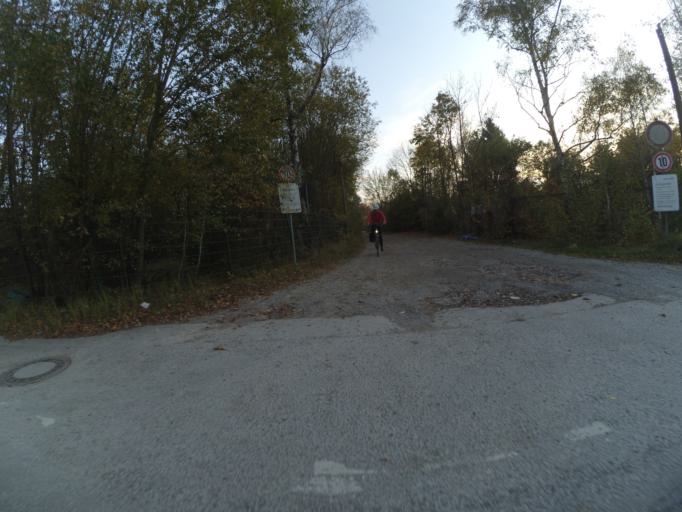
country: DE
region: Bavaria
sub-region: Upper Bavaria
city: Oberschleissheim
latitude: 48.1923
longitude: 11.5395
